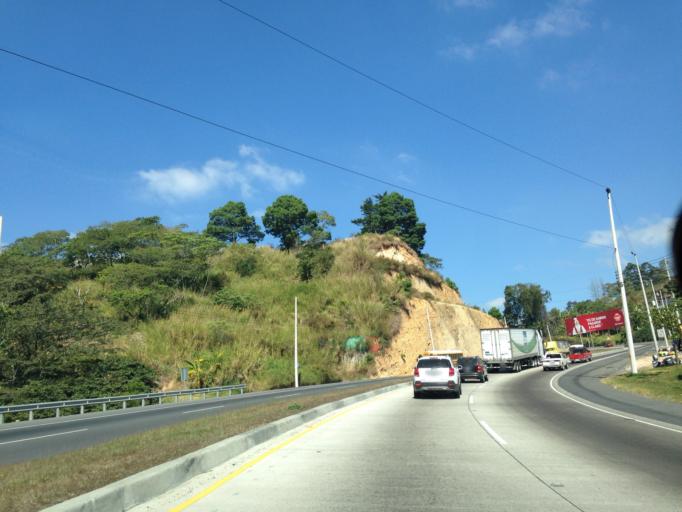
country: HN
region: Francisco Morazan
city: El Lolo
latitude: 14.1339
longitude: -87.2677
